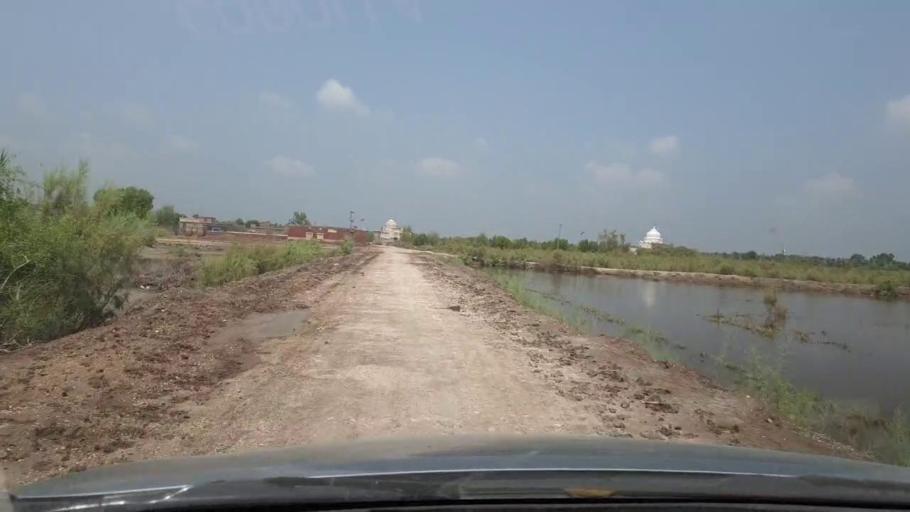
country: PK
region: Sindh
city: Khairpur
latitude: 27.4778
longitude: 68.6953
